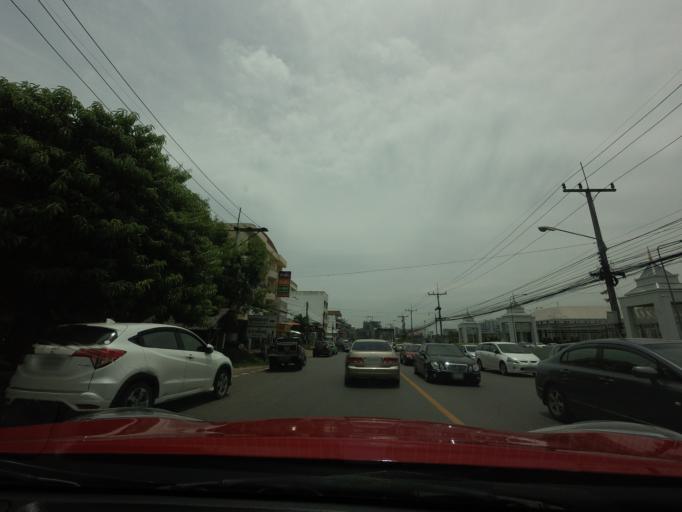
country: TH
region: Songkhla
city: Hat Yai
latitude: 7.0003
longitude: 100.5057
